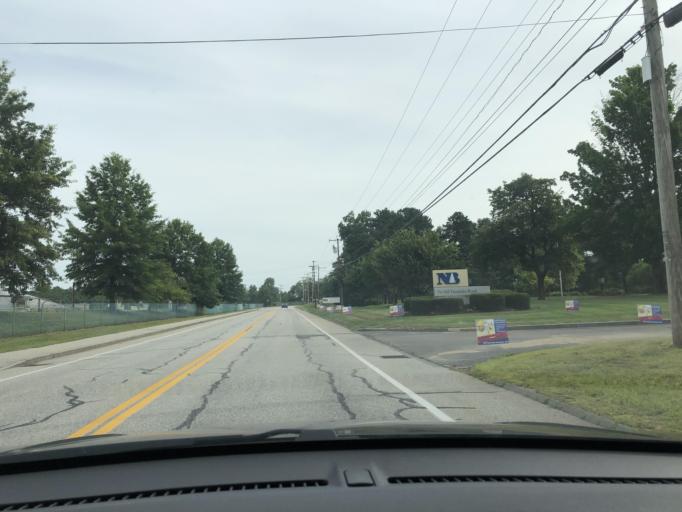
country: US
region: New Hampshire
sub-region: Merrimack County
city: Concord
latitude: 43.1992
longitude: -71.5173
